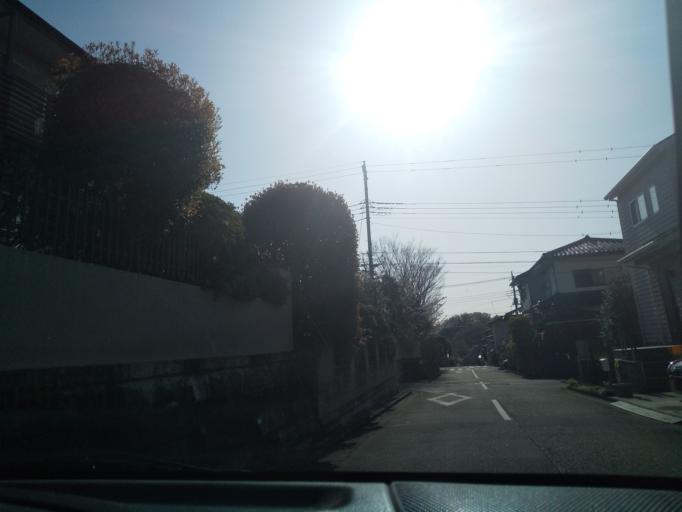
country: JP
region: Tokyo
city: Hino
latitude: 35.6517
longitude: 139.4229
